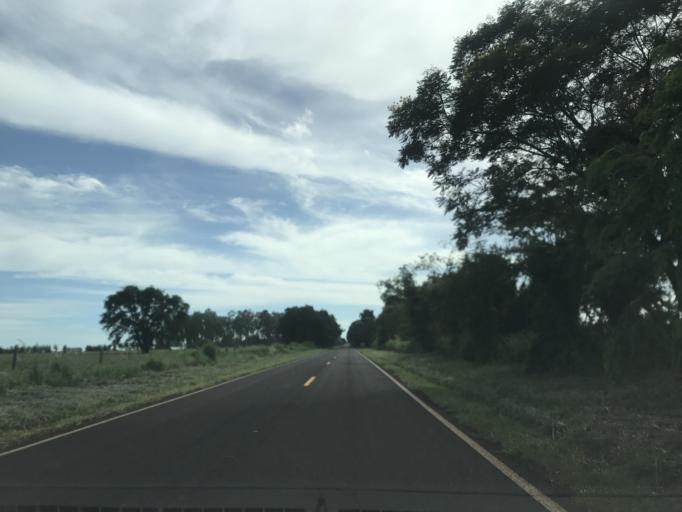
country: BR
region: Parana
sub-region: Terra Rica
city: Terra Rica
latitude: -22.7653
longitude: -52.6393
